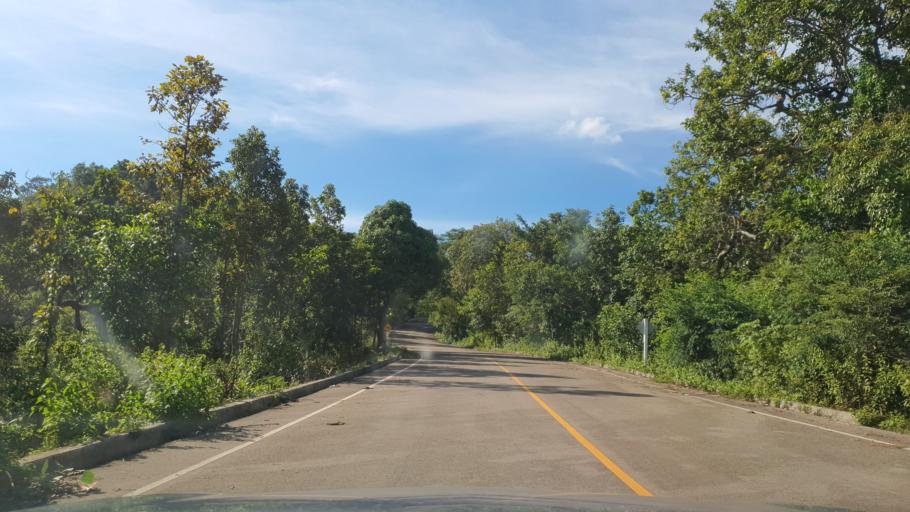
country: TH
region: Chiang Mai
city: Mae On
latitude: 18.7536
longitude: 99.2976
